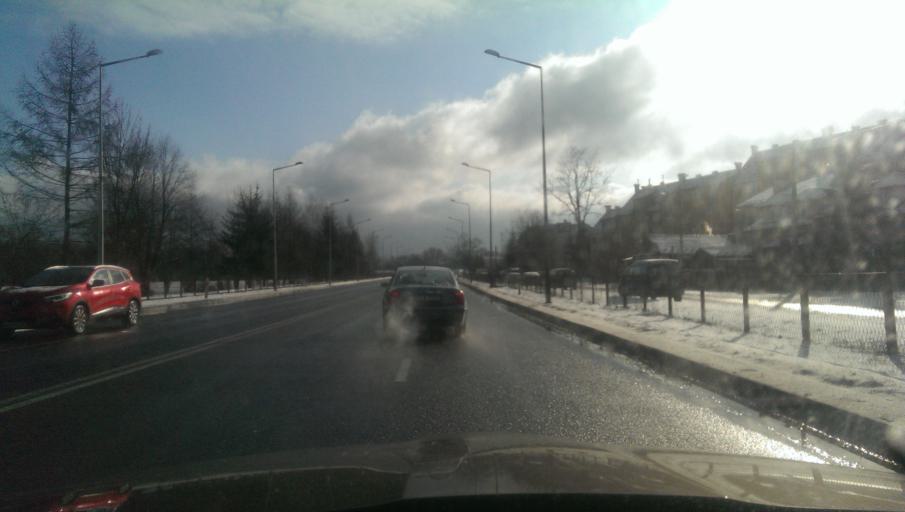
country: PL
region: Subcarpathian Voivodeship
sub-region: Powiat sanocki
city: Sanok
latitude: 49.5593
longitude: 22.2132
